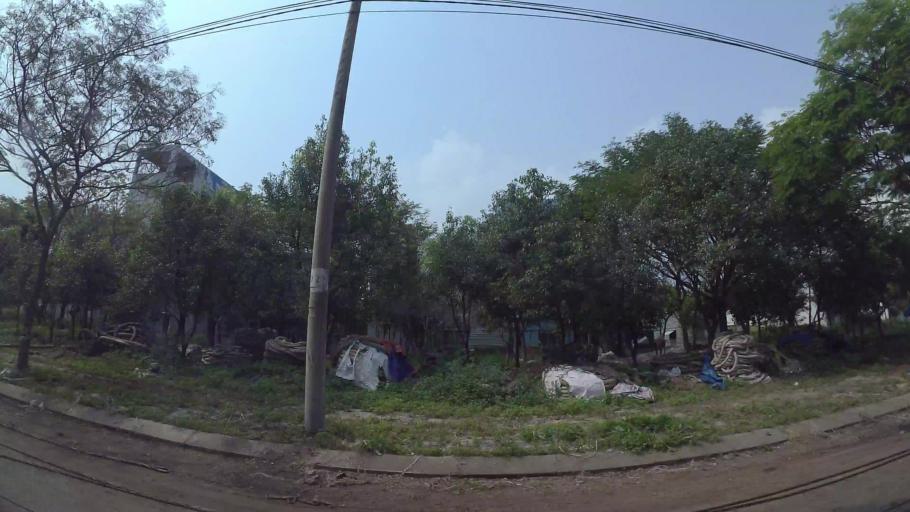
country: VN
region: Da Nang
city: Da Nang
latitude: 16.0919
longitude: 108.2389
